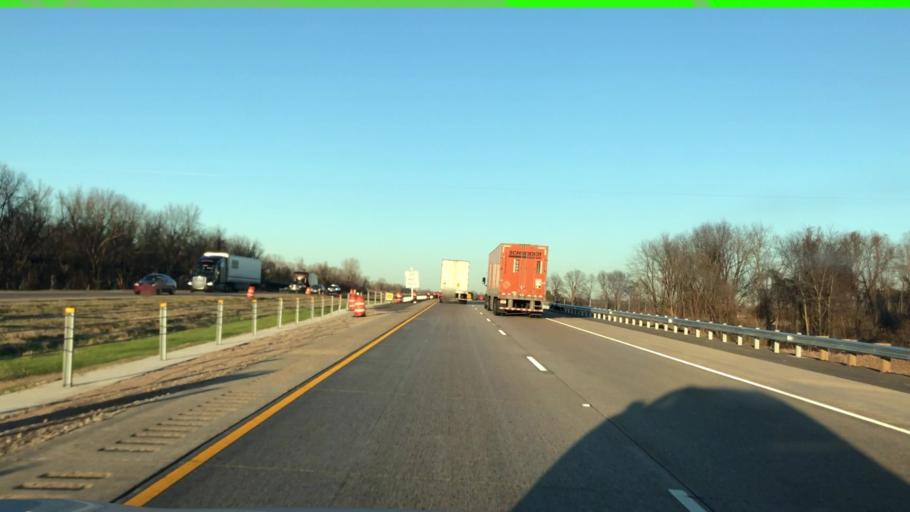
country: US
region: Arkansas
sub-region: Miller County
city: Texarkana
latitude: 33.5876
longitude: -93.8379
